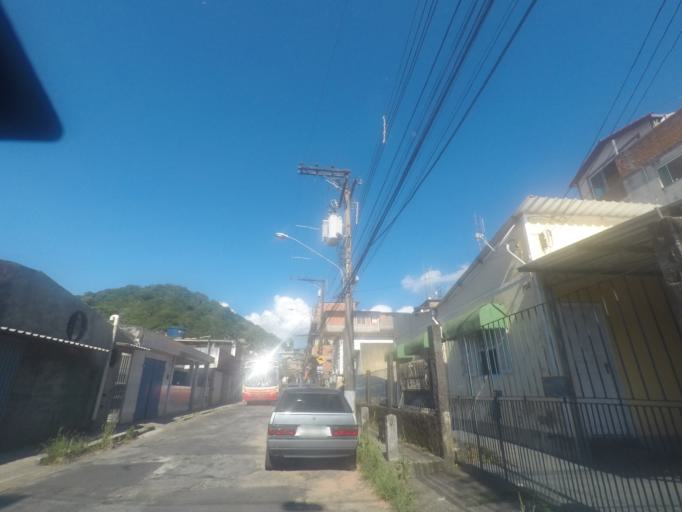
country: BR
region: Rio de Janeiro
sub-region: Petropolis
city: Petropolis
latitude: -22.5459
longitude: -43.2033
